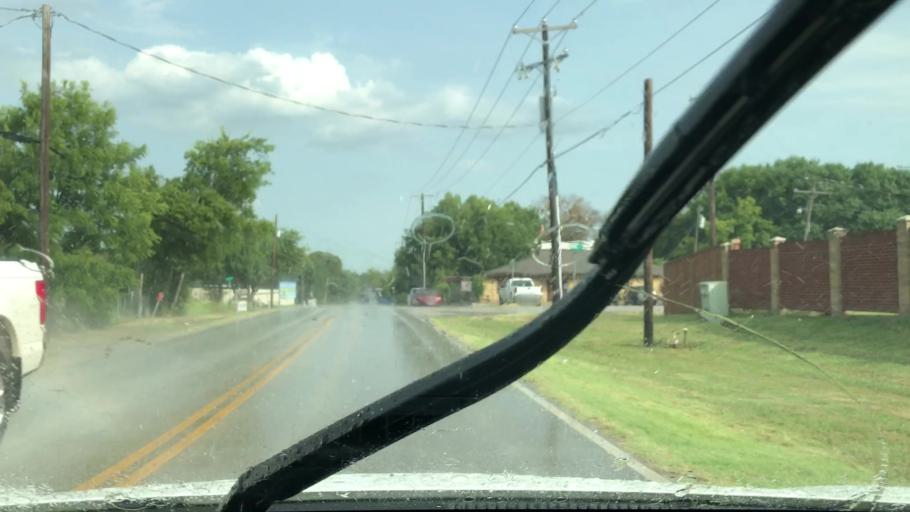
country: US
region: Texas
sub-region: Collin County
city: Wylie
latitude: 32.9582
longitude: -96.5288
